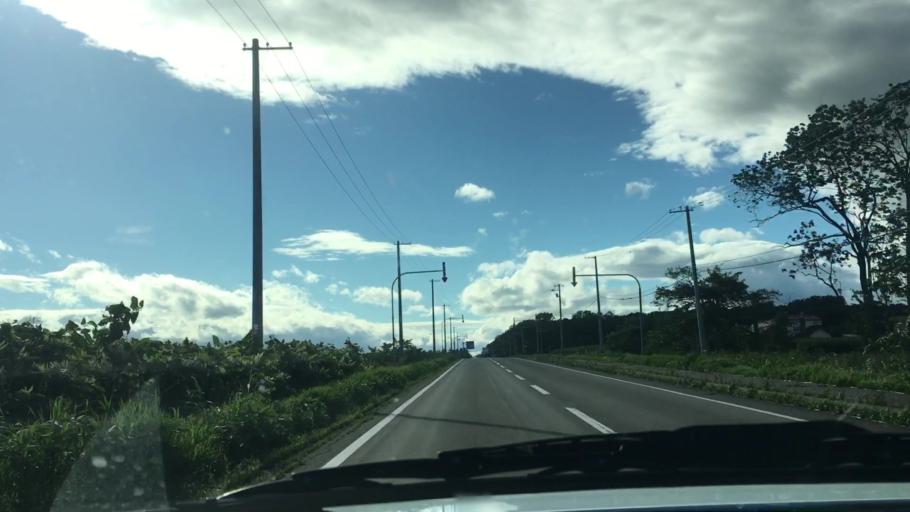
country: JP
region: Hokkaido
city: Otofuke
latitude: 43.1547
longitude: 143.1947
